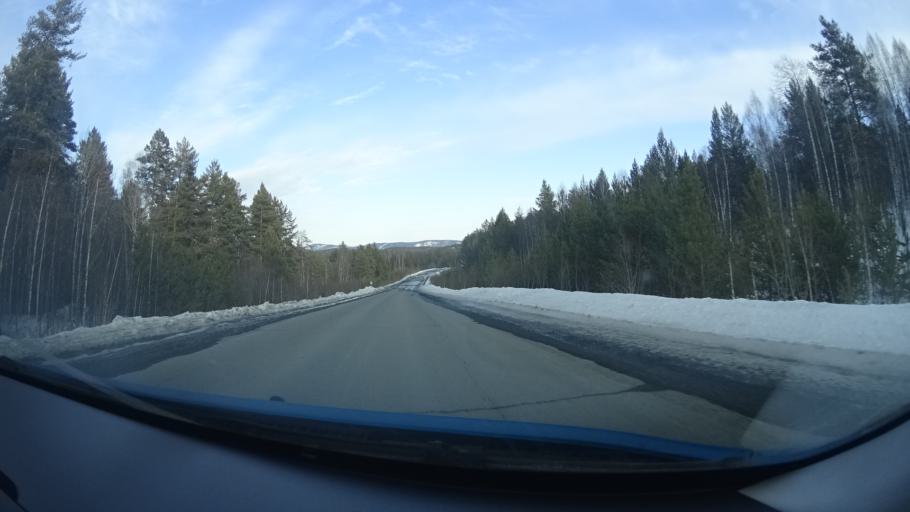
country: RU
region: Bashkortostan
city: Lomovka
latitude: 53.5240
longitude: 58.2812
